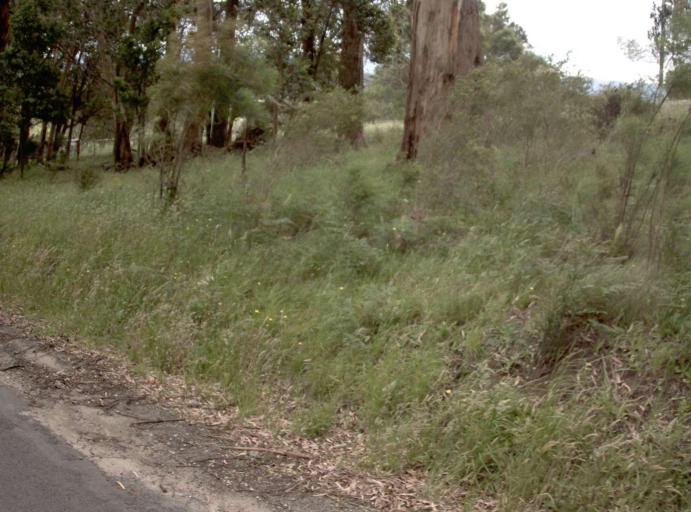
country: AU
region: Victoria
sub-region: Latrobe
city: Moe
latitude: -37.9929
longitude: 146.1461
